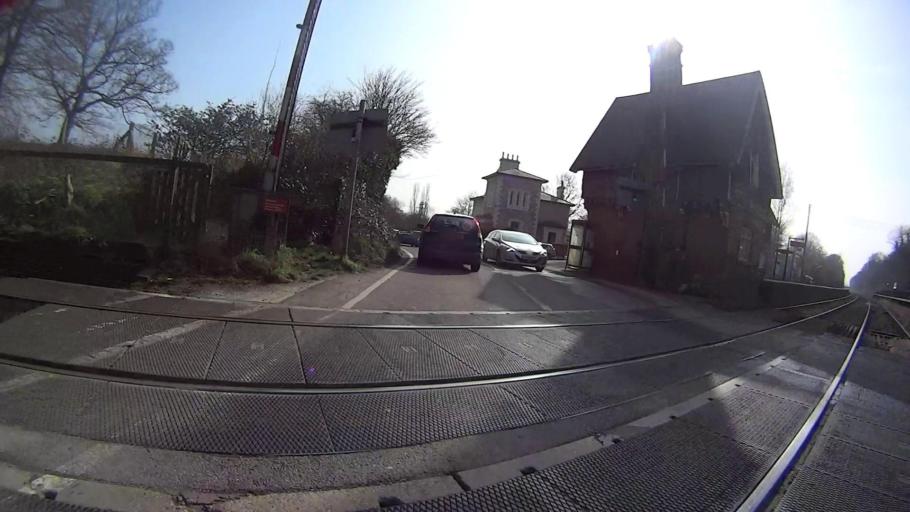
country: GB
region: England
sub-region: Surrey
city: Headley
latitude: 51.2483
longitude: -0.2667
